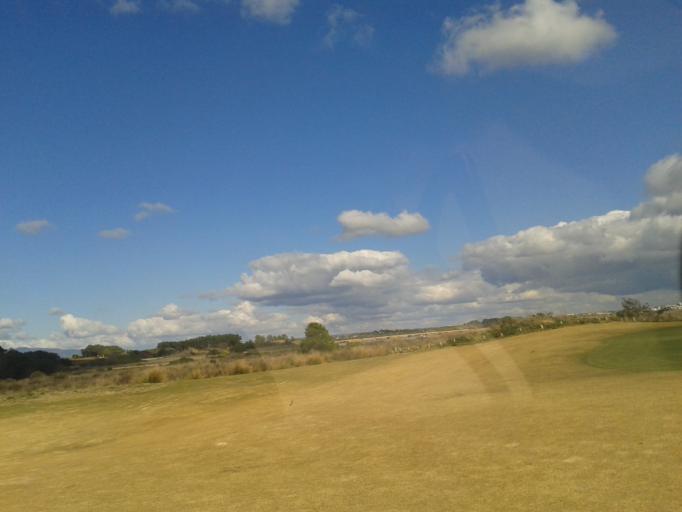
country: PT
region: Faro
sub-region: Lagos
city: Lagos
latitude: 37.1210
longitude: -8.6371
